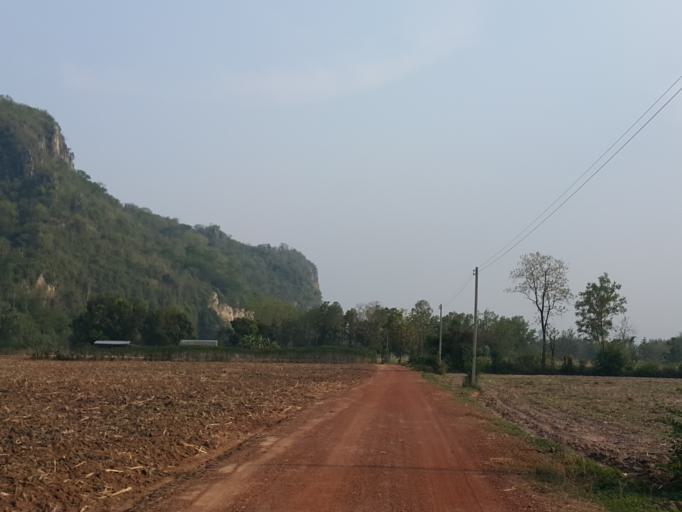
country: TH
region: Uthai Thani
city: Huai Khot
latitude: 15.3245
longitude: 99.6771
